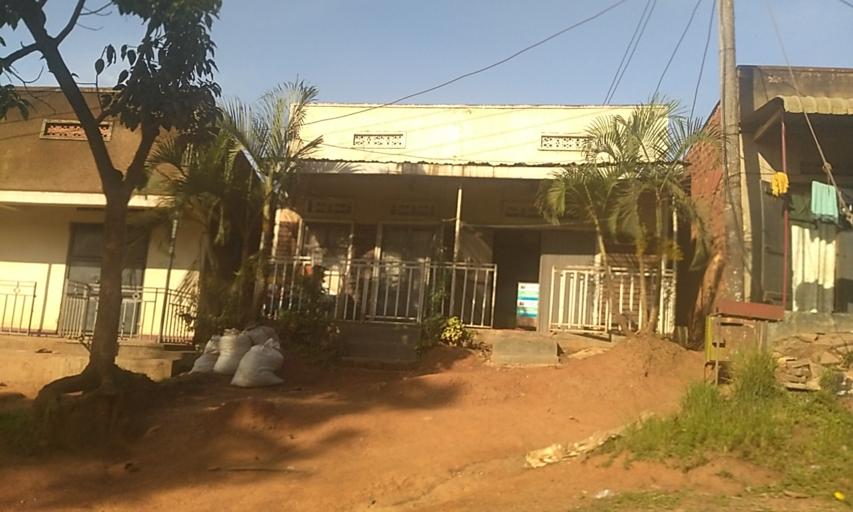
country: UG
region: Central Region
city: Kampala Central Division
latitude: 0.3220
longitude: 32.5437
